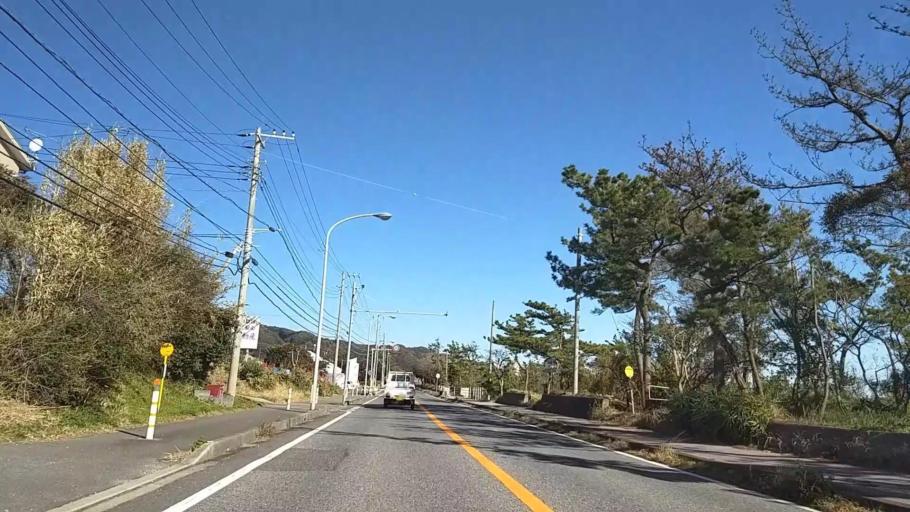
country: JP
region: Chiba
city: Kawaguchi
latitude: 35.0437
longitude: 140.0228
